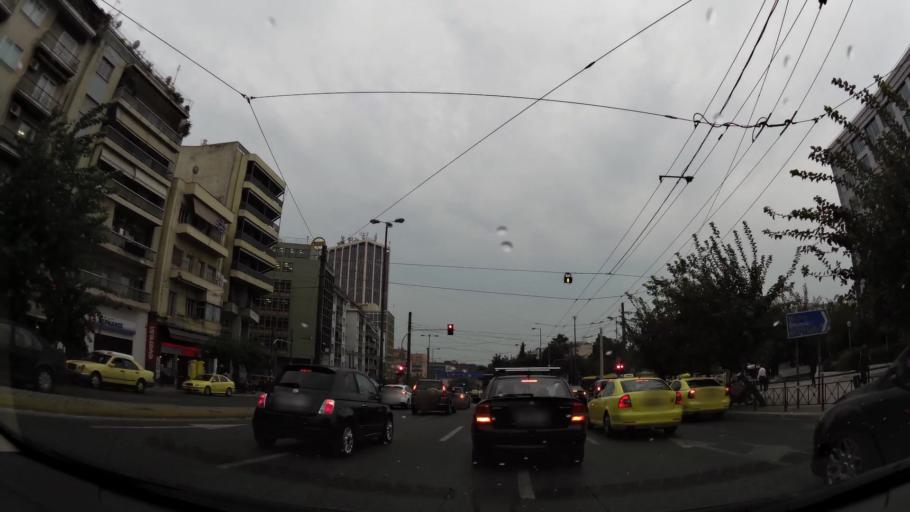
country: GR
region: Attica
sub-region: Nomarchia Athinas
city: Kaisariani
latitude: 37.9869
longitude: 23.7616
